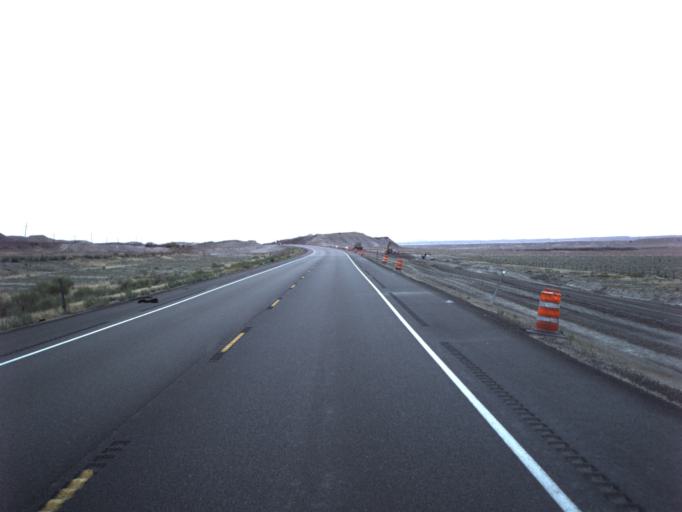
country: US
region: Utah
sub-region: Carbon County
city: East Carbon City
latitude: 39.0401
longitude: -110.3075
